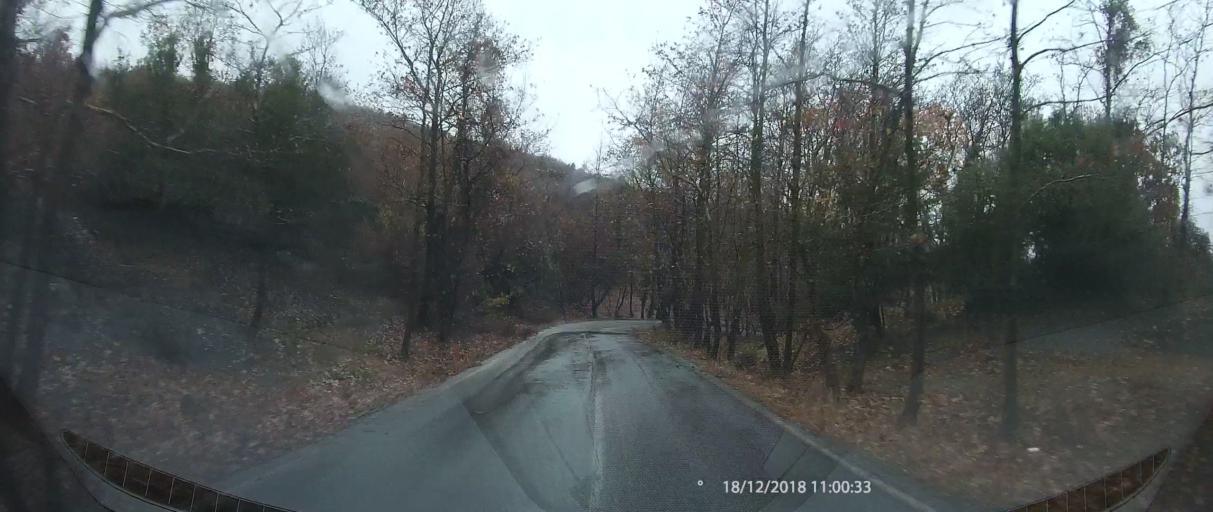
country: GR
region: Central Macedonia
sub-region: Nomos Pierias
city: Kato Milia
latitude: 40.1992
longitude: 22.3166
